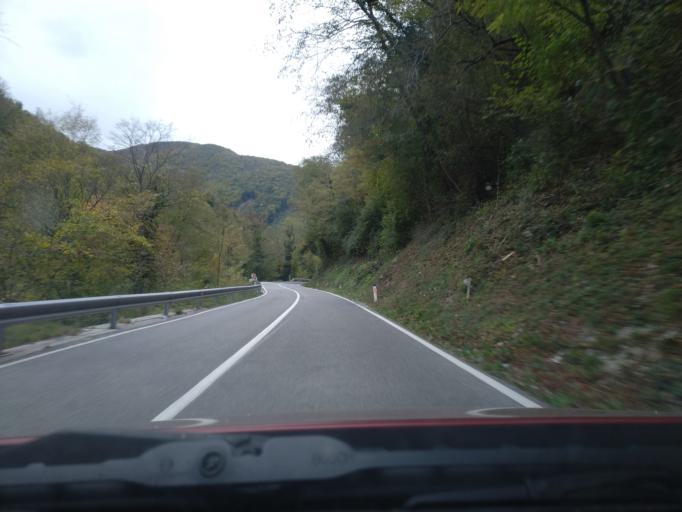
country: SI
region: Tolmin
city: Tolmin
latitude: 46.1329
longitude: 13.7168
